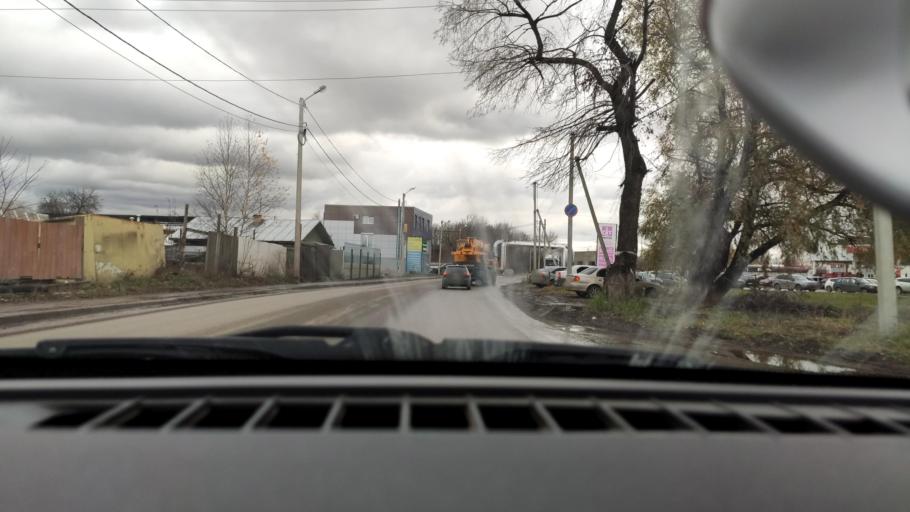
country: RU
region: Perm
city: Kondratovo
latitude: 57.9537
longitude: 56.1352
